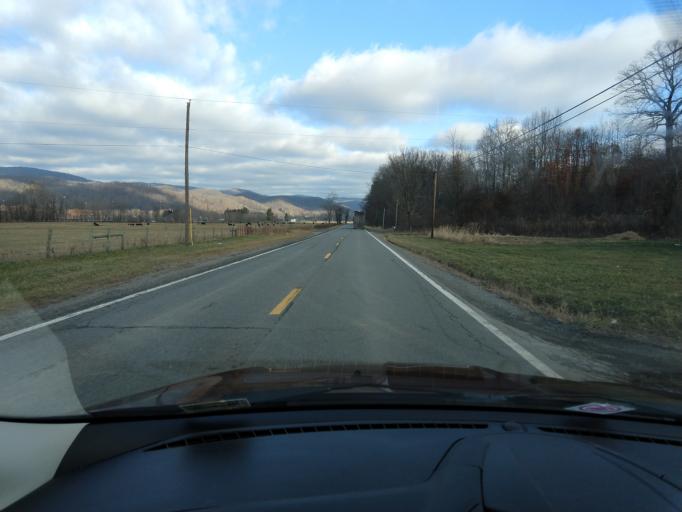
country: US
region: West Virginia
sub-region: Randolph County
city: Elkins
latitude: 38.6877
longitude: -79.9739
